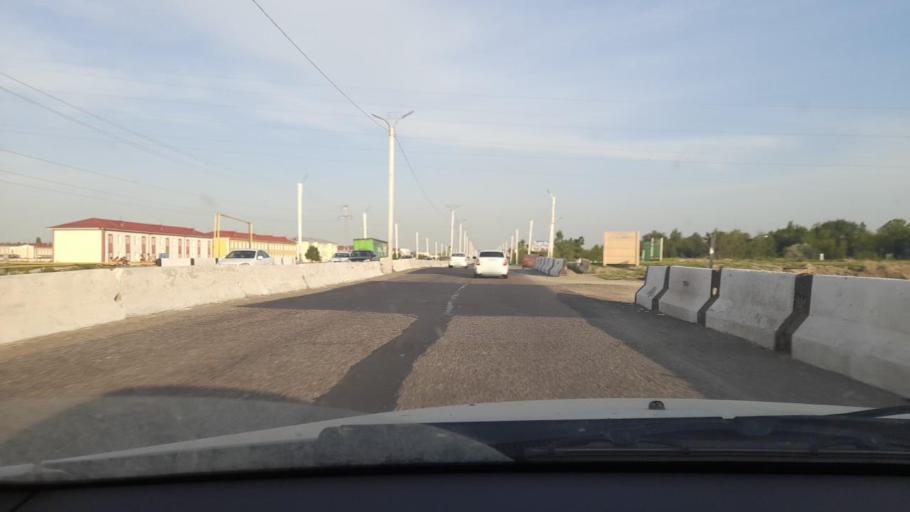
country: KZ
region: Ongtustik Qazaqstan
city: Myrzakent
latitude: 40.5503
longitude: 68.4027
